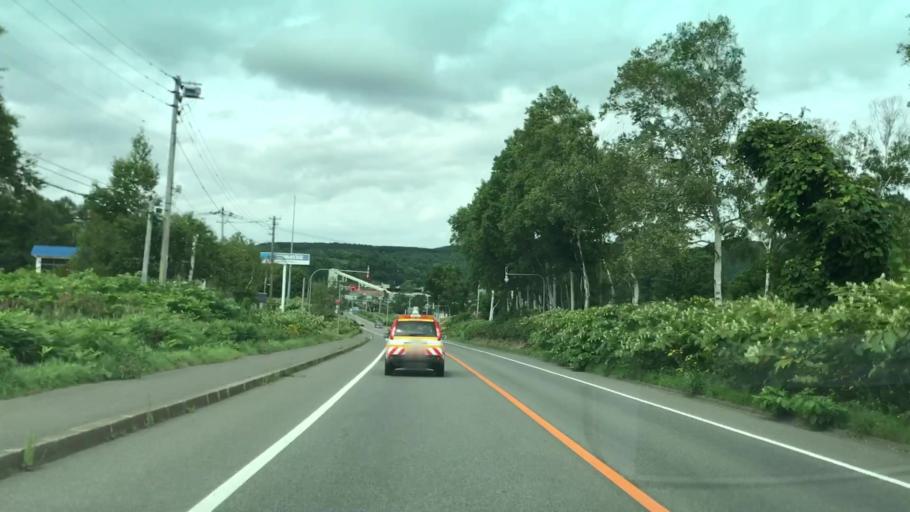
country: JP
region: Hokkaido
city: Niseko Town
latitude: 42.9166
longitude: 140.7480
